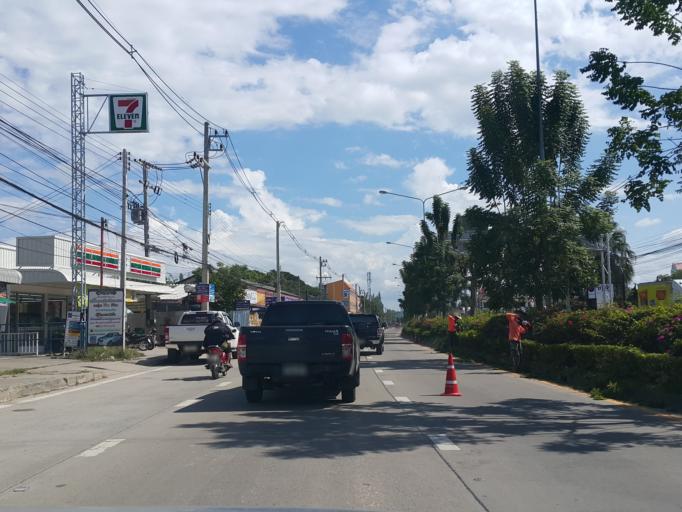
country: TH
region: Chiang Mai
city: San Sai
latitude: 18.8055
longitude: 99.0297
